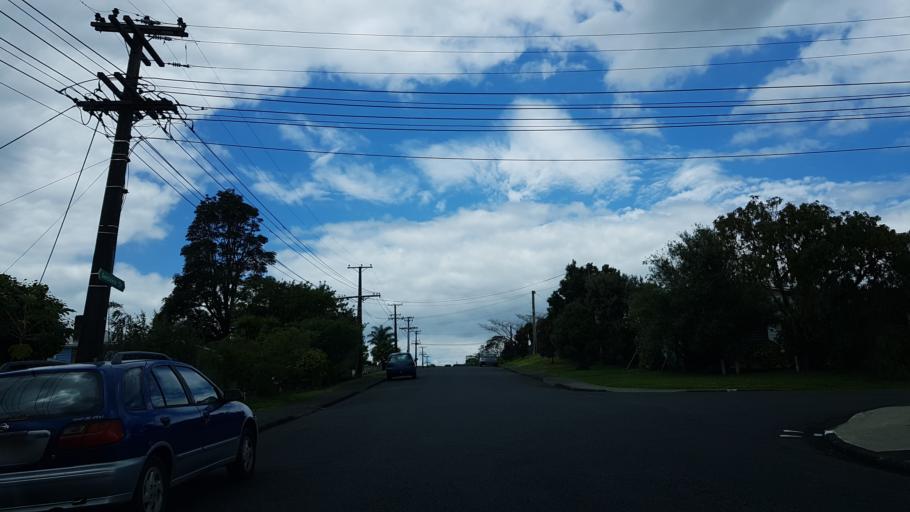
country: NZ
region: Auckland
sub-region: Auckland
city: North Shore
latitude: -36.7949
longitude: 174.6854
